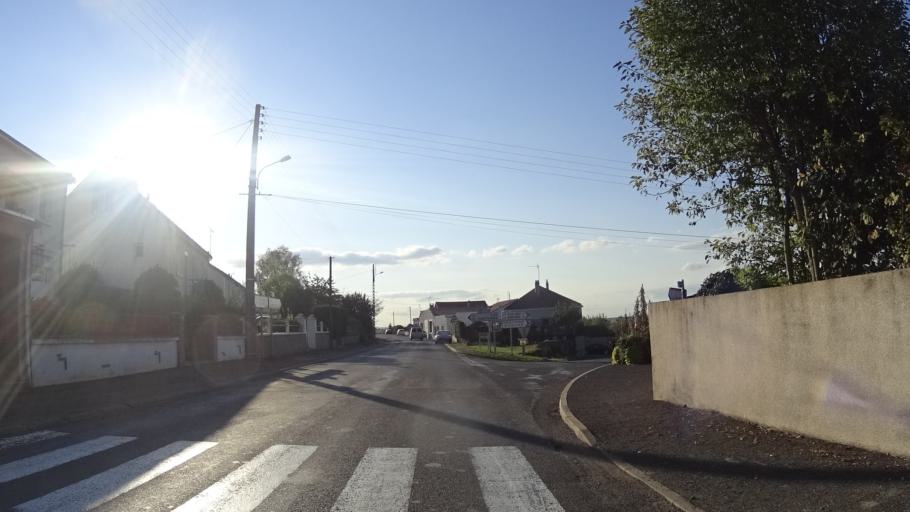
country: FR
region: Pays de la Loire
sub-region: Departement de Maine-et-Loire
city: Bouzille
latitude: 47.3399
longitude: -1.1128
